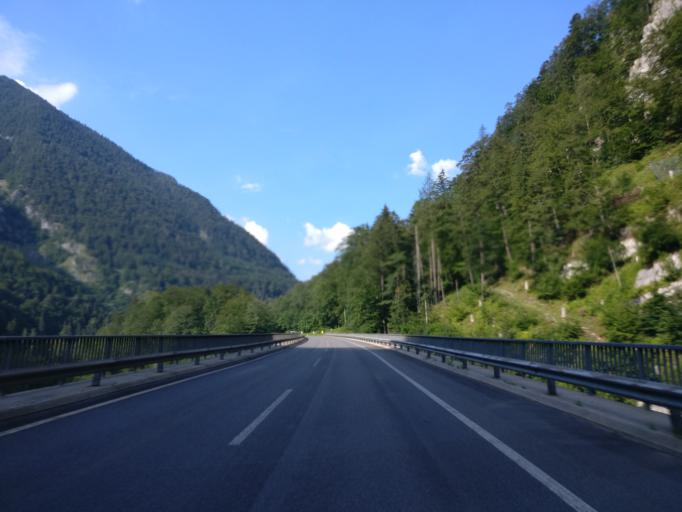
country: AT
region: Styria
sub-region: Politischer Bezirk Leoben
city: Hieflau
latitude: 47.5995
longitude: 14.7267
